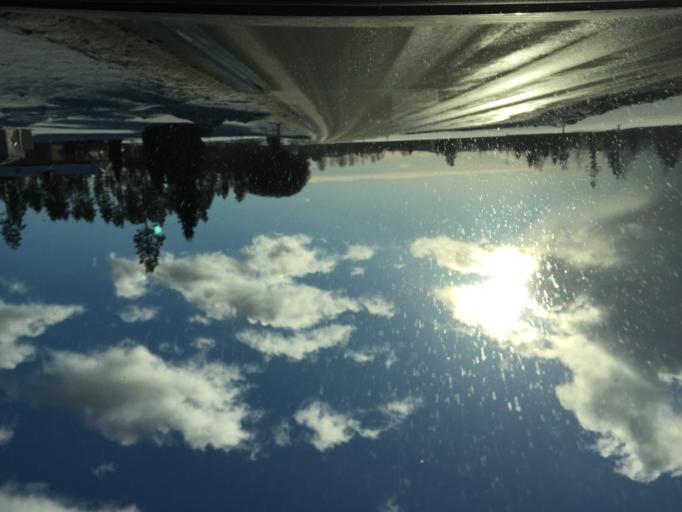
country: NO
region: Hedmark
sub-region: Sor-Odal
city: Skarnes
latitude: 60.2343
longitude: 11.6680
